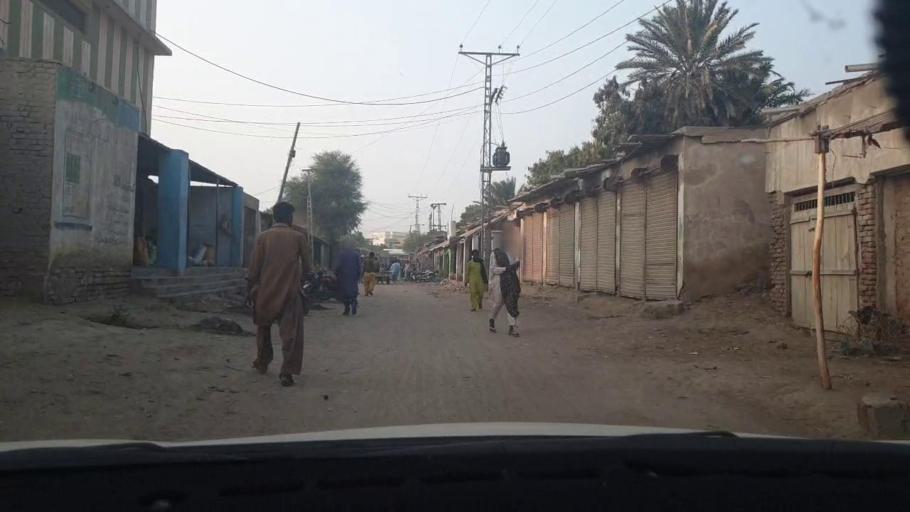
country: PK
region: Sindh
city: Bulri
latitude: 24.8616
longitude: 68.3319
